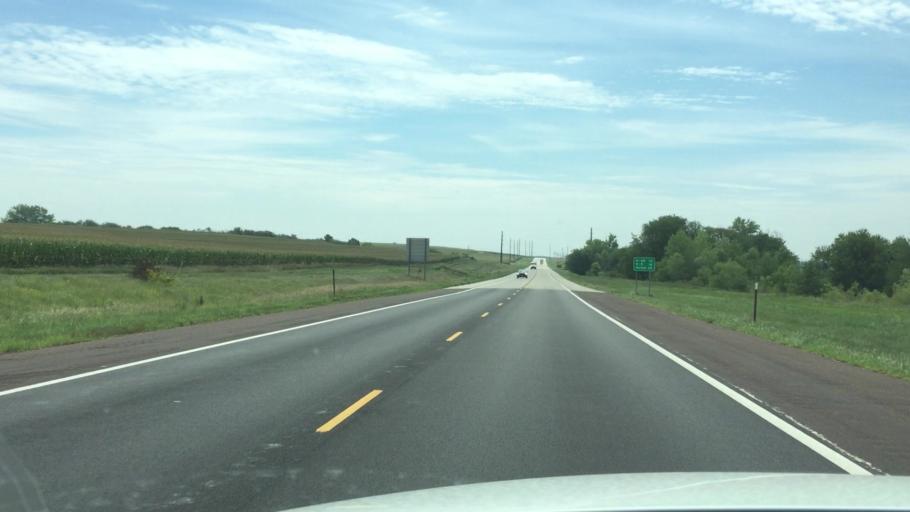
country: US
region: Kansas
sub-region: Nemaha County
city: Sabetha
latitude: 39.8319
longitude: -95.7330
